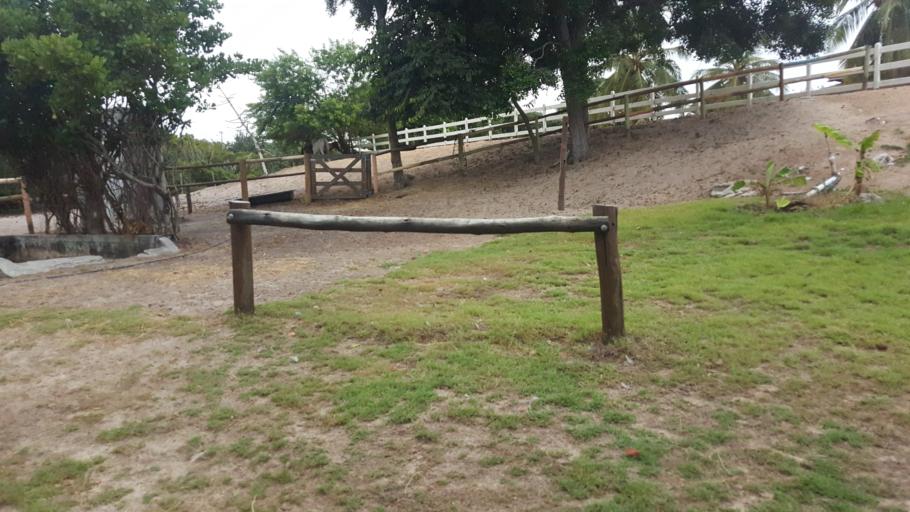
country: BR
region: Bahia
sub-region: Mata De Sao Joao
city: Mata de Sao Joao
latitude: -12.4250
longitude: -37.9240
